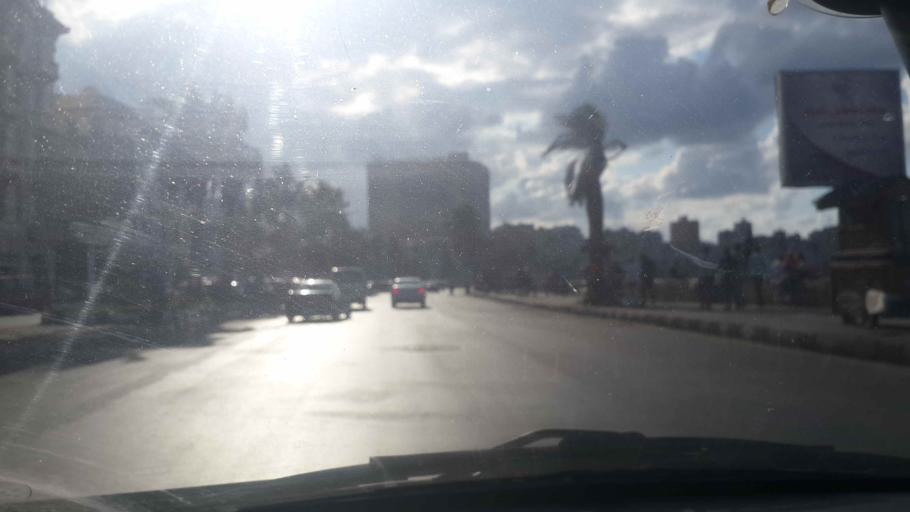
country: EG
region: Alexandria
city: Alexandria
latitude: 31.2006
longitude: 29.8961
